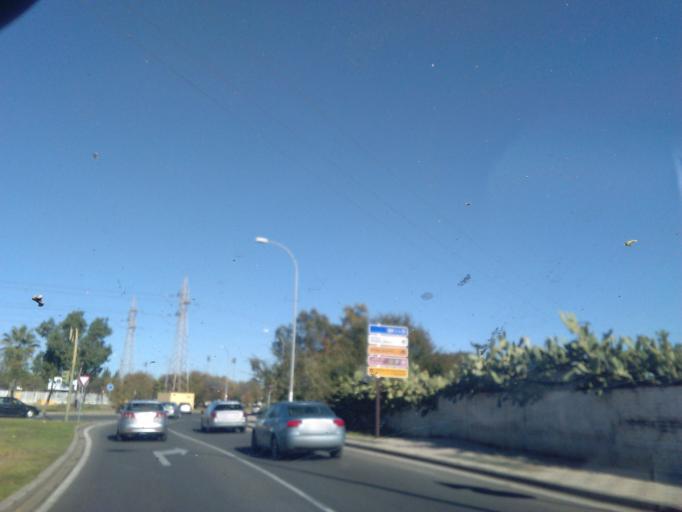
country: ES
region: Andalusia
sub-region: Provincia de Sevilla
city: Sevilla
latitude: 37.3892
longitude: -5.9145
